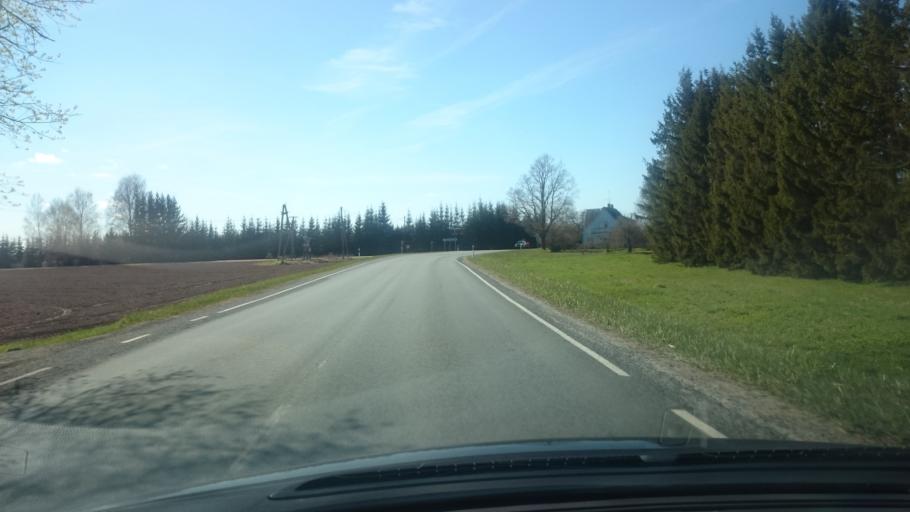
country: EE
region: Polvamaa
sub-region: Polva linn
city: Polva
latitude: 58.2254
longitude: 27.0320
